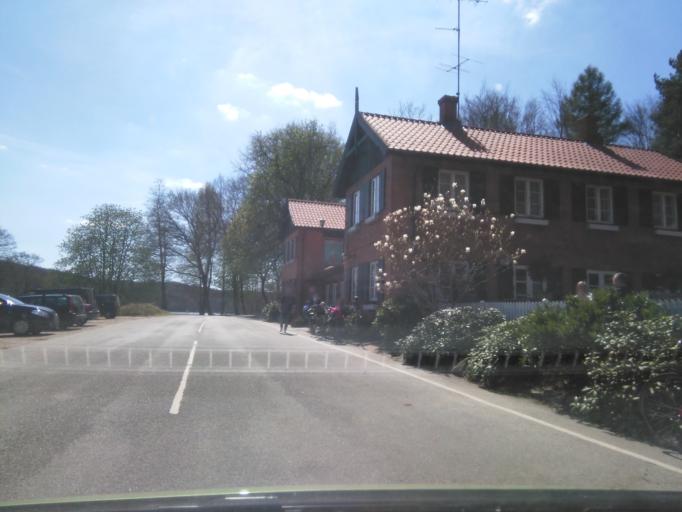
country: DK
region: Central Jutland
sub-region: Viborg Kommune
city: Viborg
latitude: 56.3889
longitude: 9.3379
